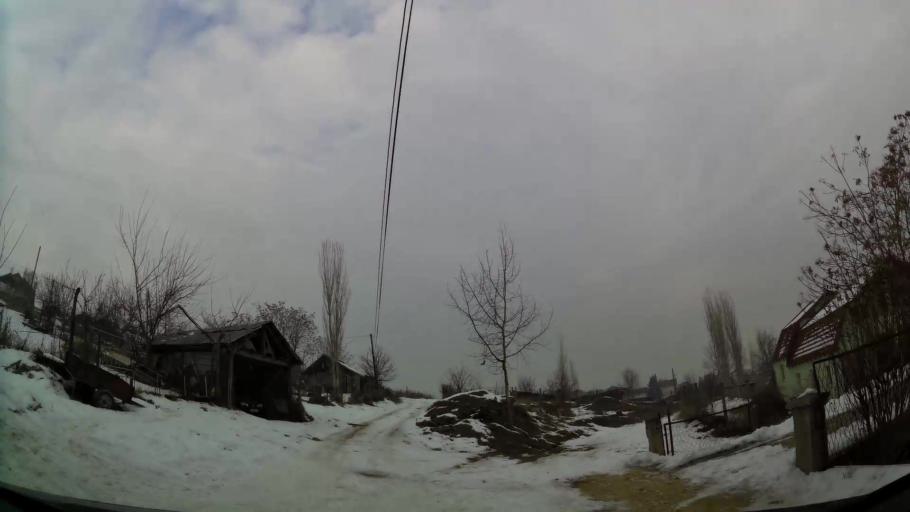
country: MK
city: Kondovo
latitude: 42.0416
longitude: 21.3442
